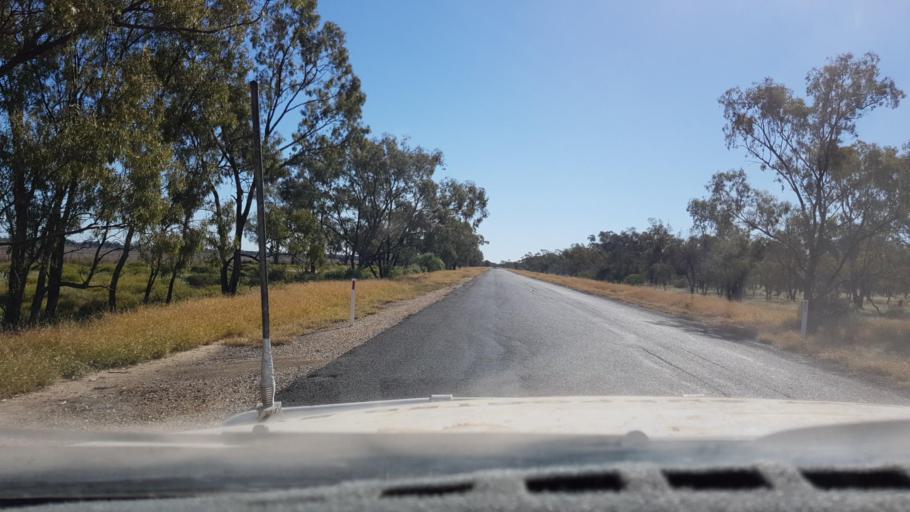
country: AU
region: New South Wales
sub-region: Walgett
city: Lightning Ridge
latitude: -29.5781
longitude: 148.6792
